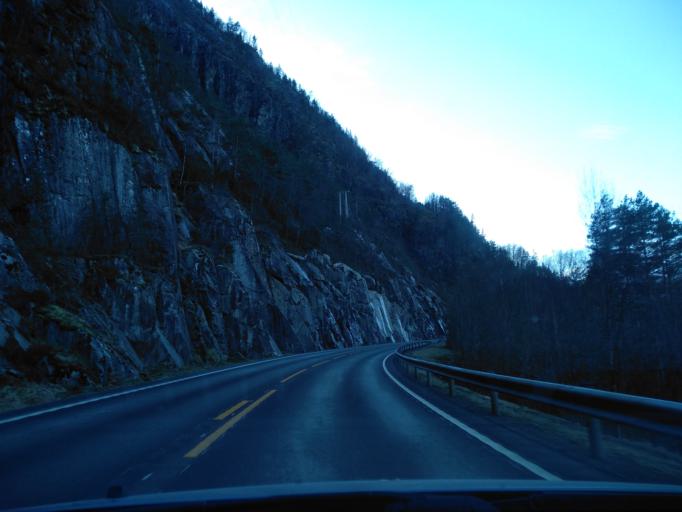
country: NO
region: Rogaland
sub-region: Sauda
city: Sauda
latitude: 59.8320
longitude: 6.2800
